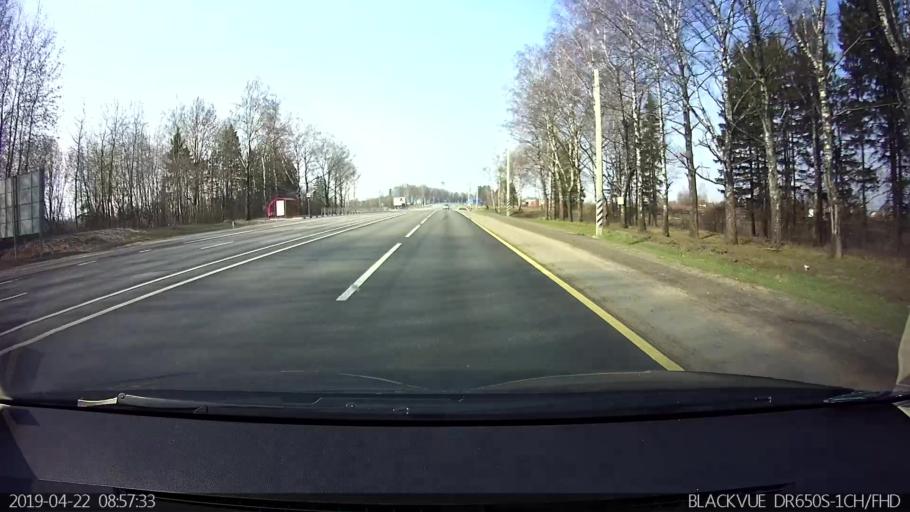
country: RU
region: Smolensk
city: Pechersk
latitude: 54.8682
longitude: 32.0146
